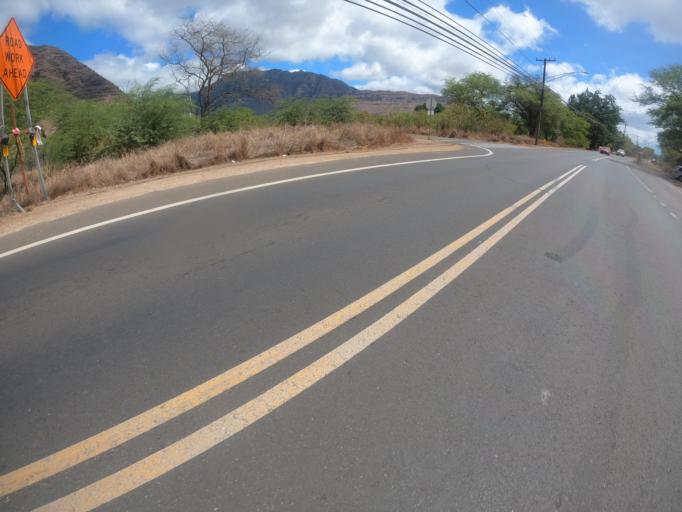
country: US
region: Hawaii
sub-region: Honolulu County
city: Makaha
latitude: 21.4767
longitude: -158.2197
